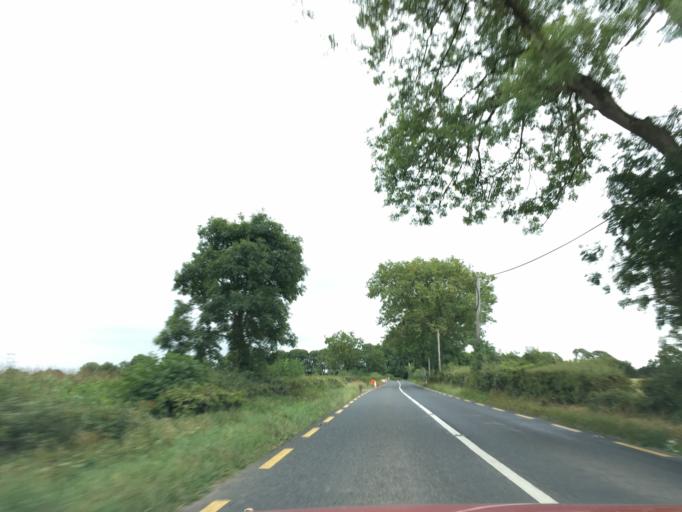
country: IE
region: Munster
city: Fethard
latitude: 52.4381
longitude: -7.7949
